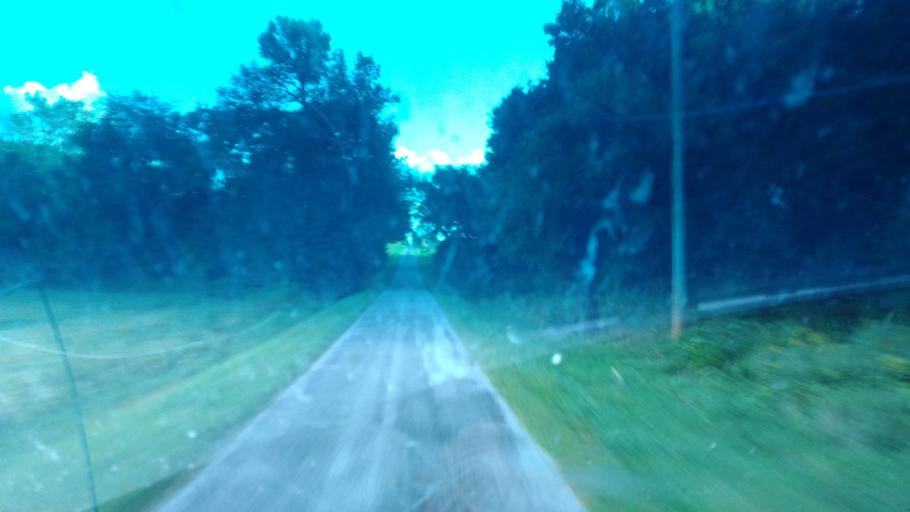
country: US
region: Ohio
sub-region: Wyandot County
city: Upper Sandusky
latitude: 40.8853
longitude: -83.1509
